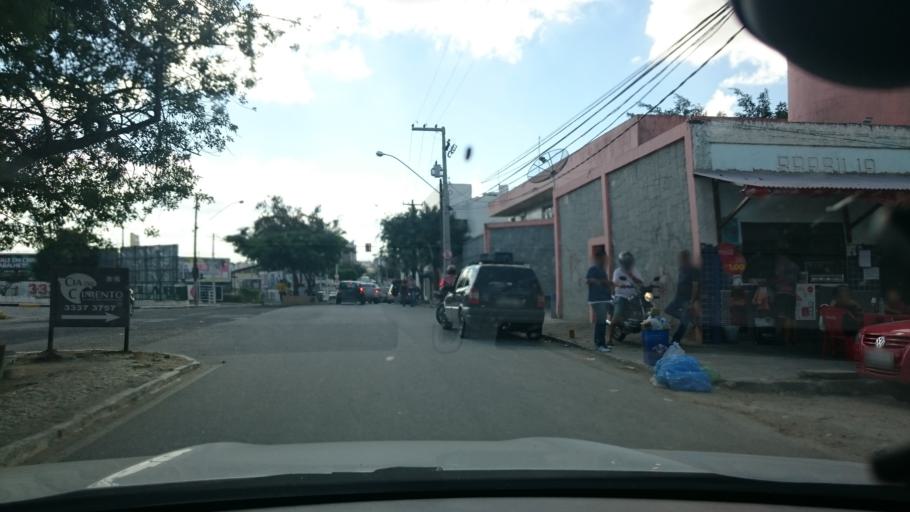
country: BR
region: Paraiba
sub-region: Campina Grande
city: Campina Grande
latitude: -7.2378
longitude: -35.8699
